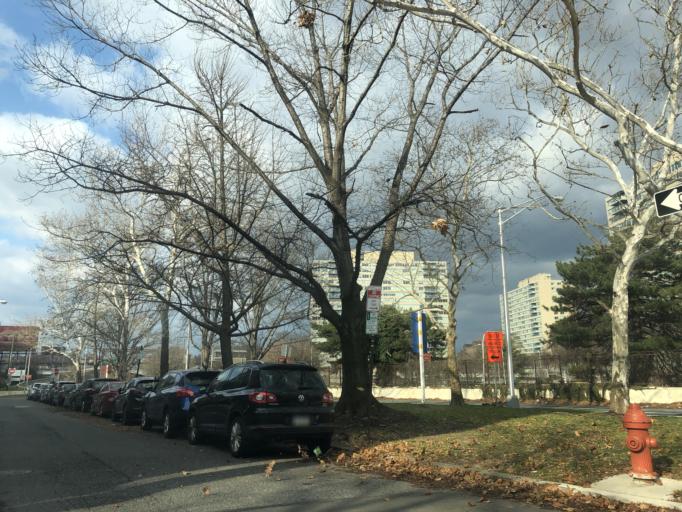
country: US
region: Pennsylvania
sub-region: Philadelphia County
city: Philadelphia
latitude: 39.9590
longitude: -75.1757
